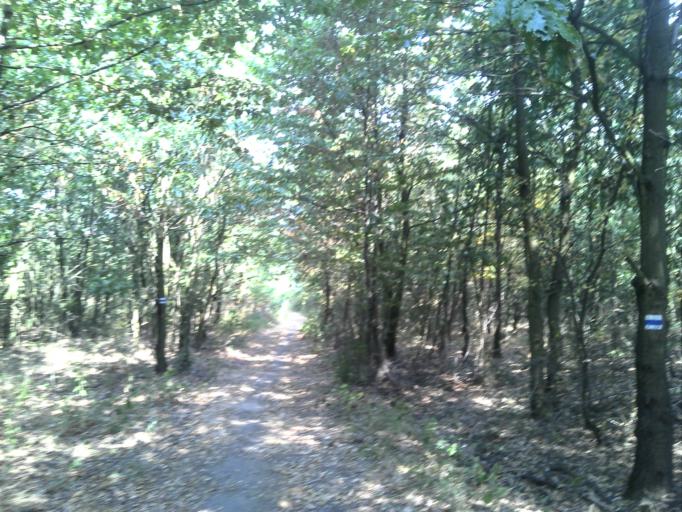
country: HU
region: Komarom-Esztergom
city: Oroszlany
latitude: 47.4328
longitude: 18.3438
